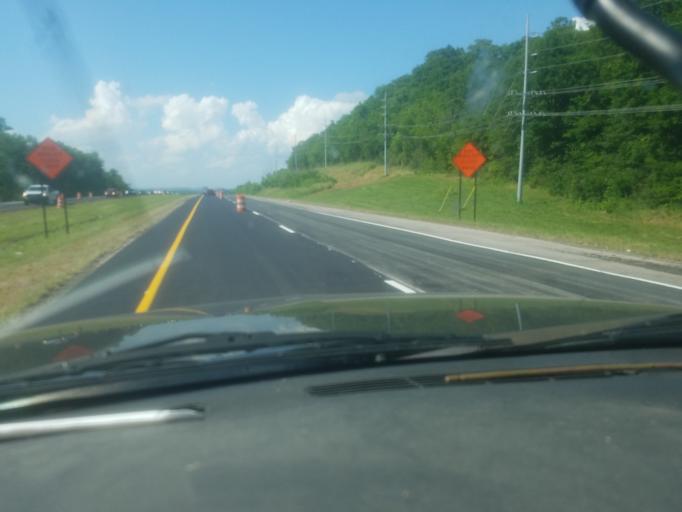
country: US
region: Tennessee
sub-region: Maury County
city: Mount Pleasant
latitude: 35.5361
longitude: -87.2214
